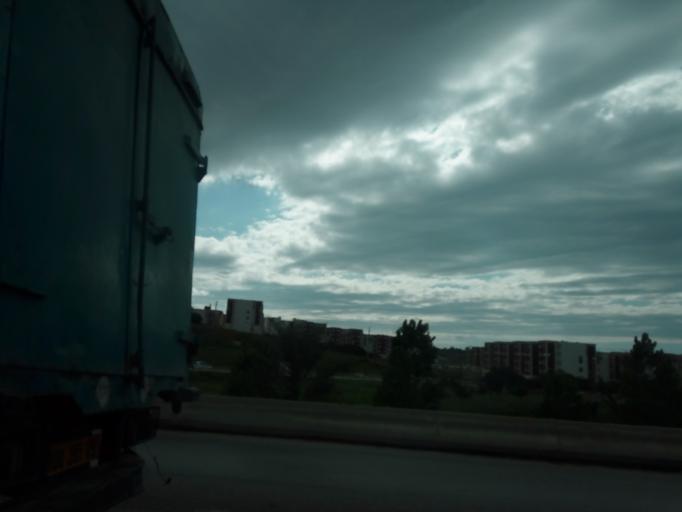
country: DZ
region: Tipaza
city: Douera
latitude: 36.6842
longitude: 2.9571
